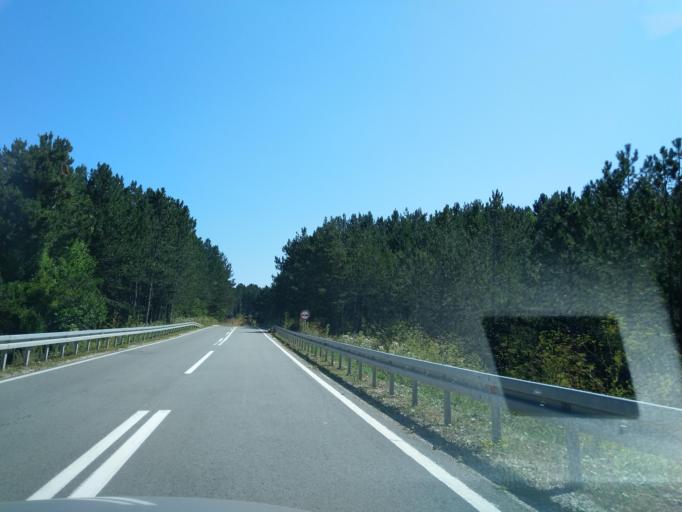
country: RS
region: Central Serbia
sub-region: Zlatiborski Okrug
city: Sjenica
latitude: 43.3063
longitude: 19.9038
